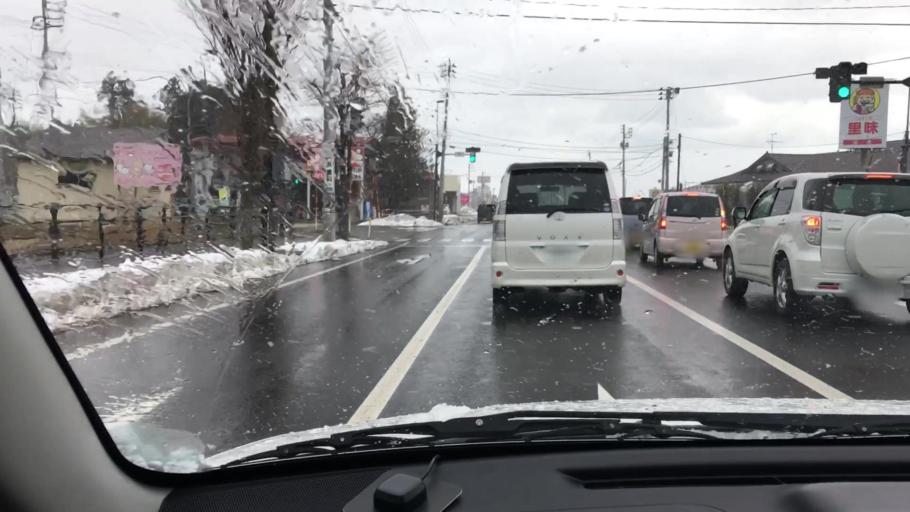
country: JP
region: Niigata
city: Joetsu
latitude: 37.1232
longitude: 138.2323
